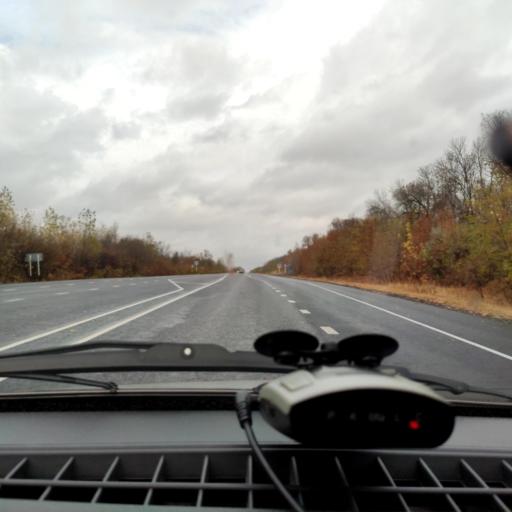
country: RU
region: Voronezj
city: Uryv-Pokrovka
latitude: 51.2308
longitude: 39.0597
